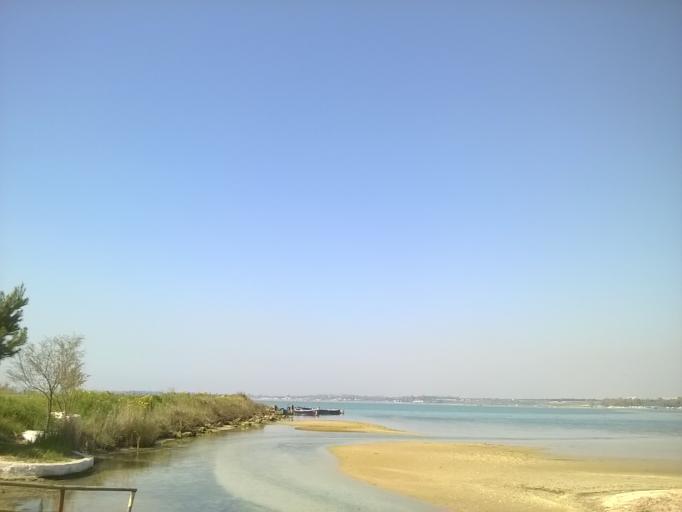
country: IT
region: Apulia
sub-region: Provincia di Taranto
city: Paolo VI
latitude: 40.4944
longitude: 17.3245
